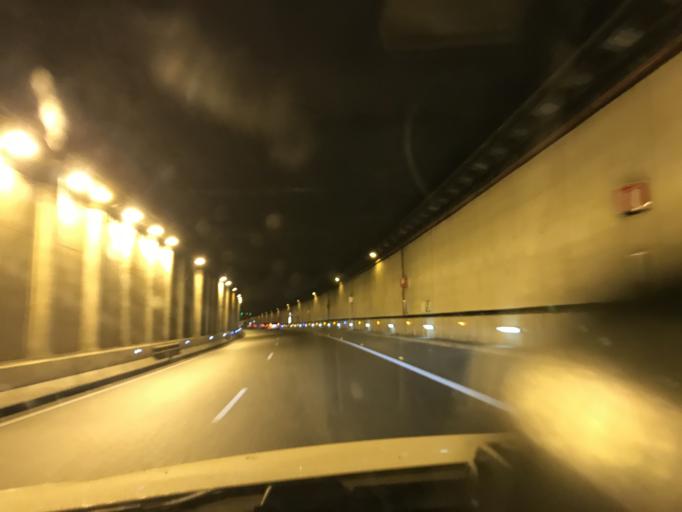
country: ES
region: Andalusia
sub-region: Provincia de Malaga
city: Benahavis
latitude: 36.4842
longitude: -4.9860
